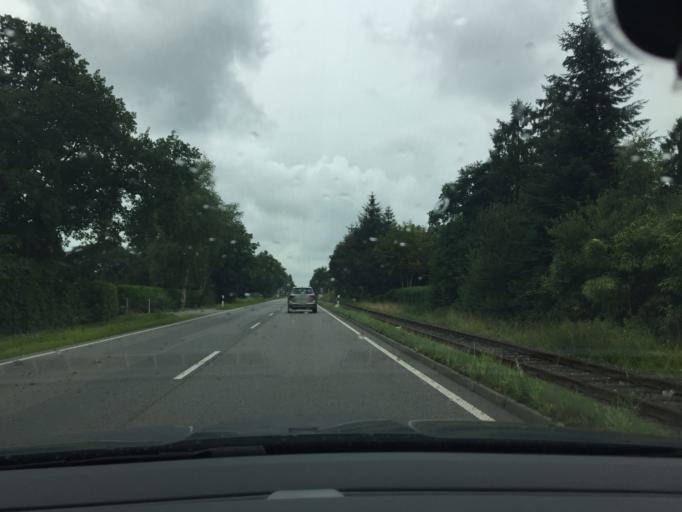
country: DE
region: Lower Saxony
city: Aurich
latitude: 53.4728
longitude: 7.4395
